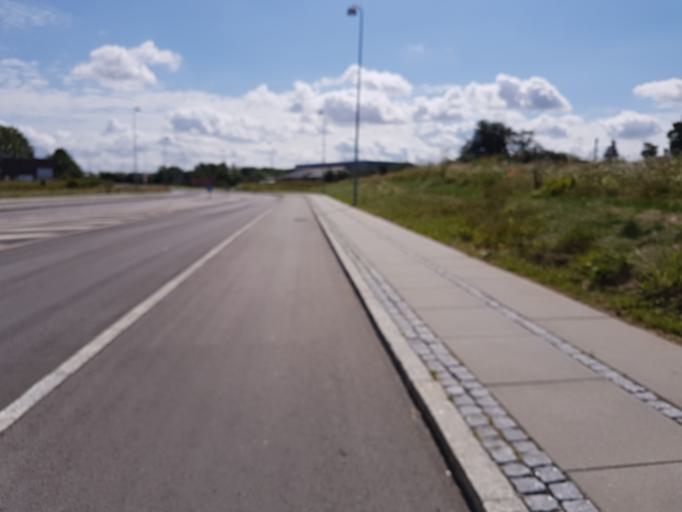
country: DK
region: Capital Region
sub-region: Egedal Kommune
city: Stenlose
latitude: 55.7768
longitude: 12.1916
